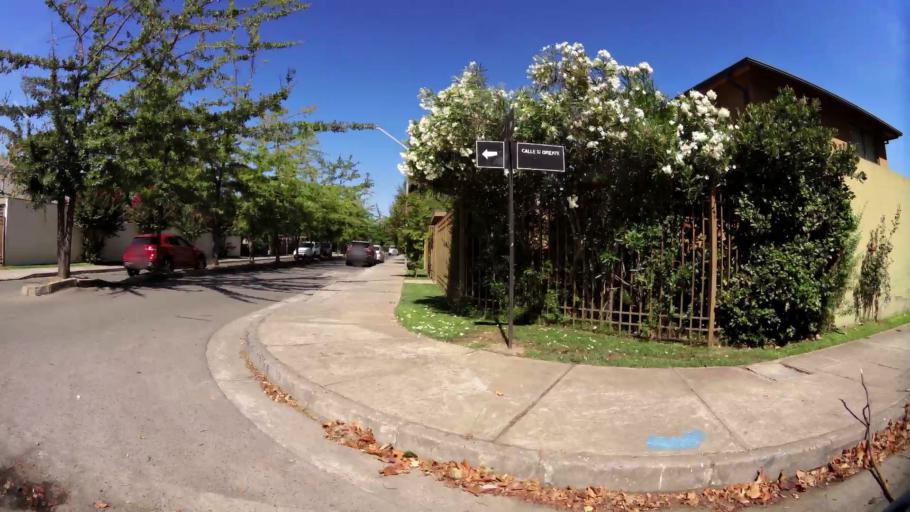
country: CL
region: Maule
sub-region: Provincia de Talca
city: Talca
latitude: -35.4358
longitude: -71.6160
